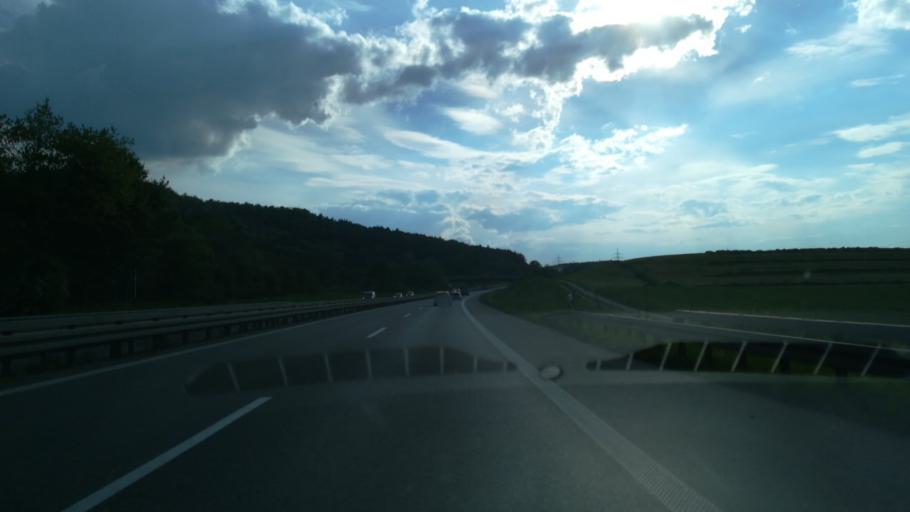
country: DE
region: Baden-Wuerttemberg
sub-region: Freiburg Region
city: Orsingen-Nenzingen
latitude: 47.8285
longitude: 8.9483
